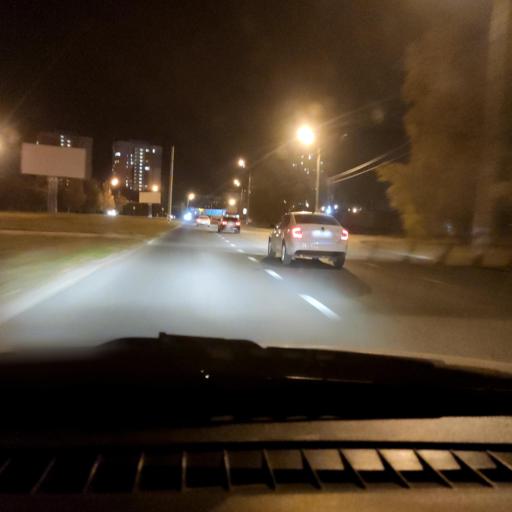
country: RU
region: Samara
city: Tol'yatti
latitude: 53.5039
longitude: 49.2586
